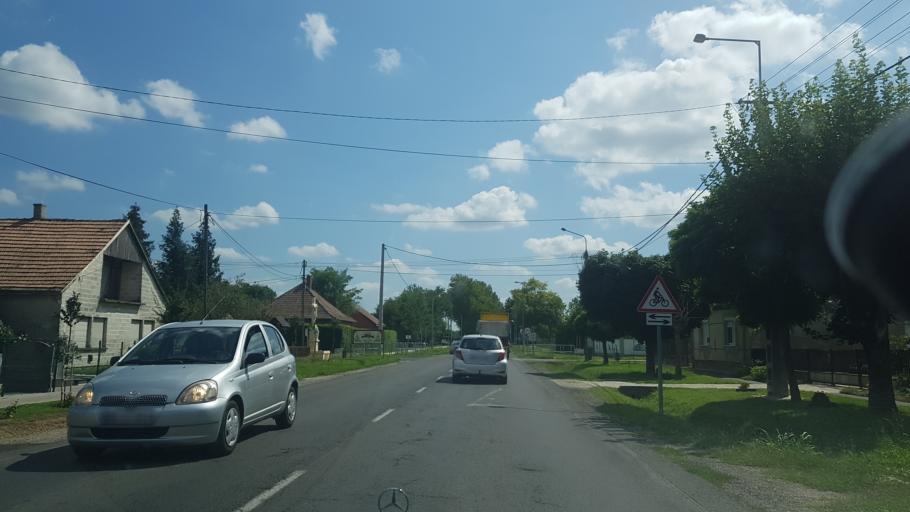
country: HU
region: Somogy
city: Kethely
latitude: 46.6356
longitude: 17.3958
